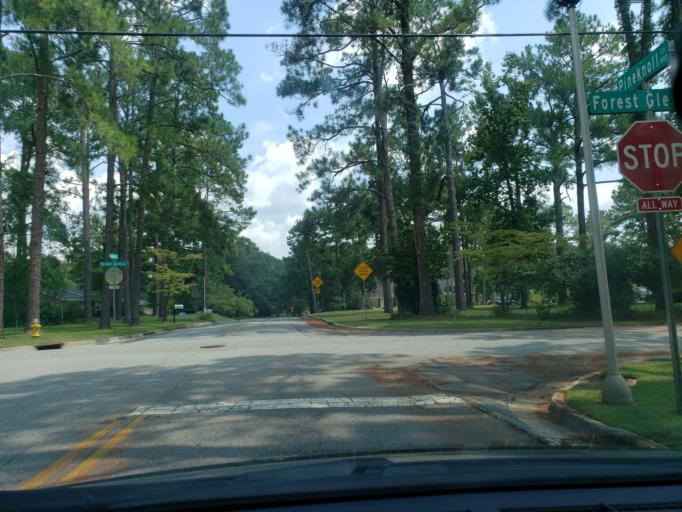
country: US
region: Georgia
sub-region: Dougherty County
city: Albany
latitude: 31.5955
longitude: -84.1974
